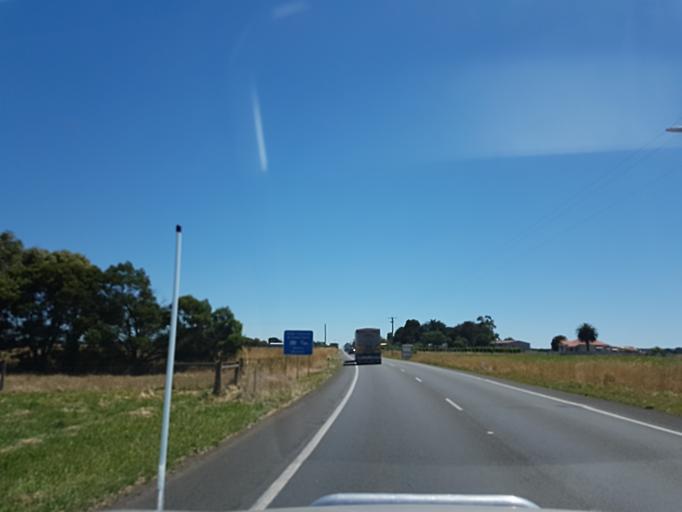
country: AU
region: Victoria
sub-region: Colac-Otway
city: Colac
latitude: -38.3344
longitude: 143.5407
